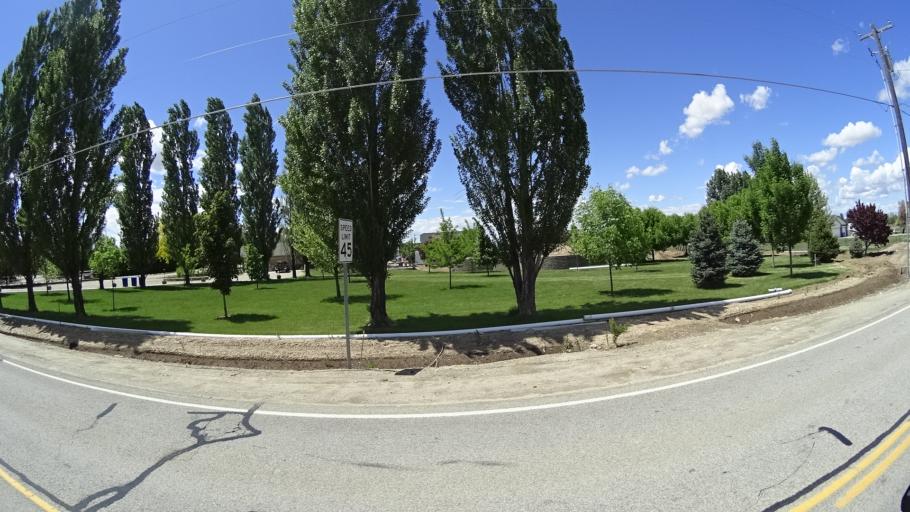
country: US
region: Idaho
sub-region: Ada County
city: Meridian
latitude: 43.5797
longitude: -116.4338
